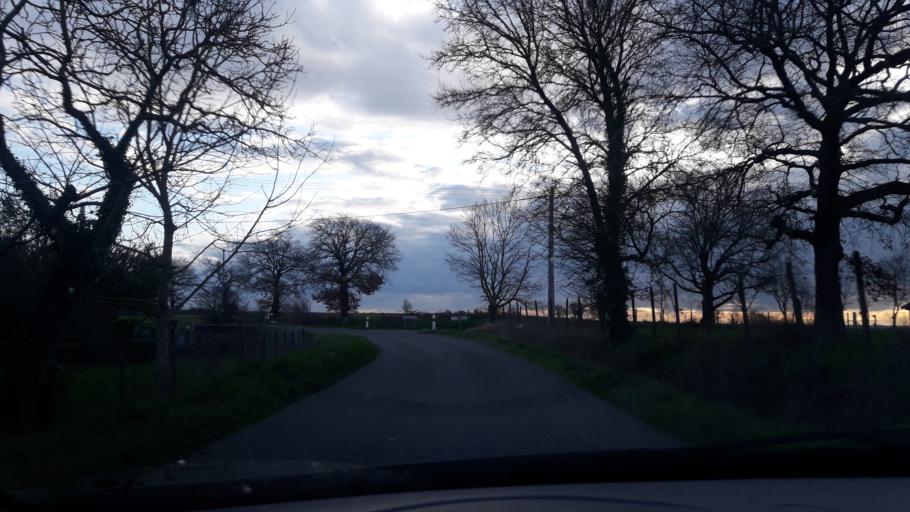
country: FR
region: Midi-Pyrenees
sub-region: Departement du Gers
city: Gimont
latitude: 43.6468
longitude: 1.0010
